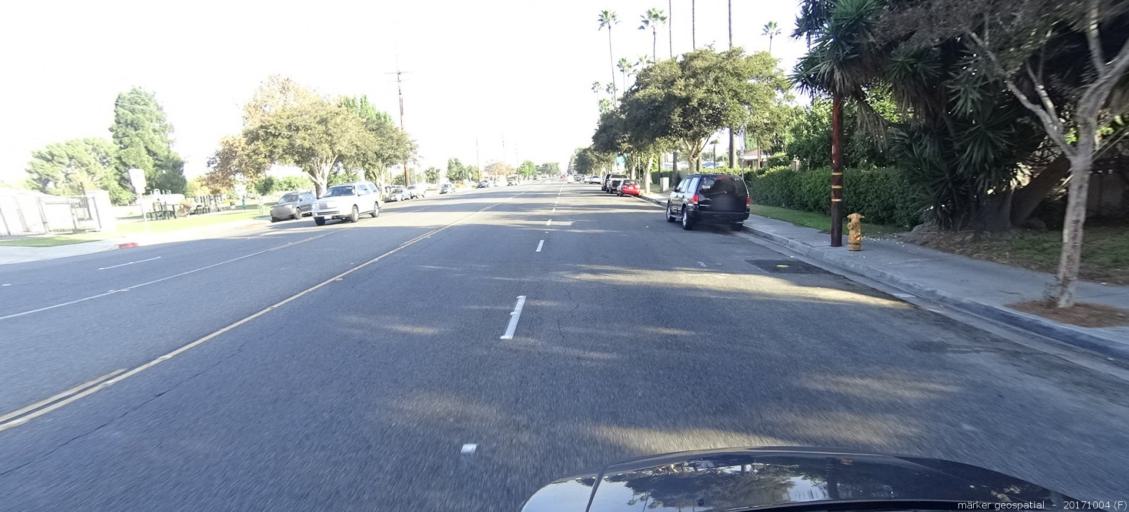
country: US
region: California
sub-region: Orange County
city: Garden Grove
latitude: 33.7797
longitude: -117.9061
